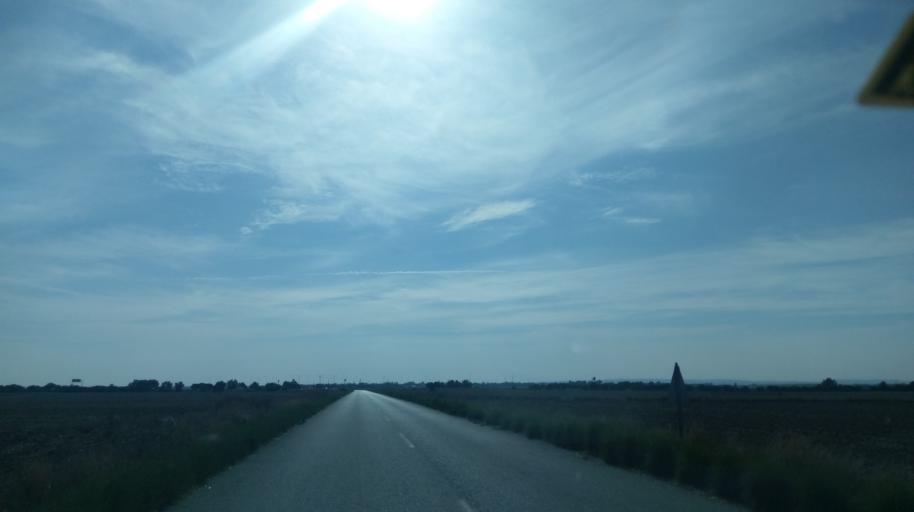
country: CY
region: Ammochostos
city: Lefkonoiko
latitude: 35.1882
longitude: 33.6994
